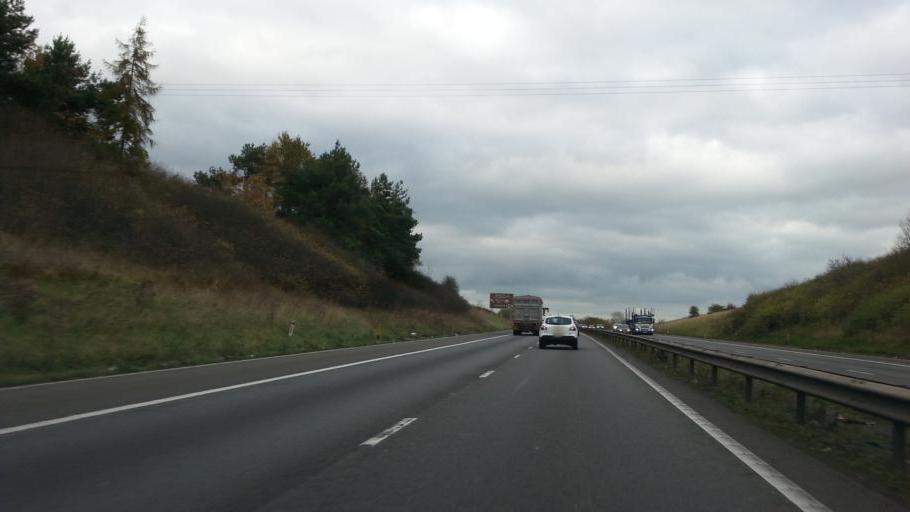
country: GB
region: England
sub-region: Derbyshire
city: Netherseal
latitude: 52.6724
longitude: -1.5606
